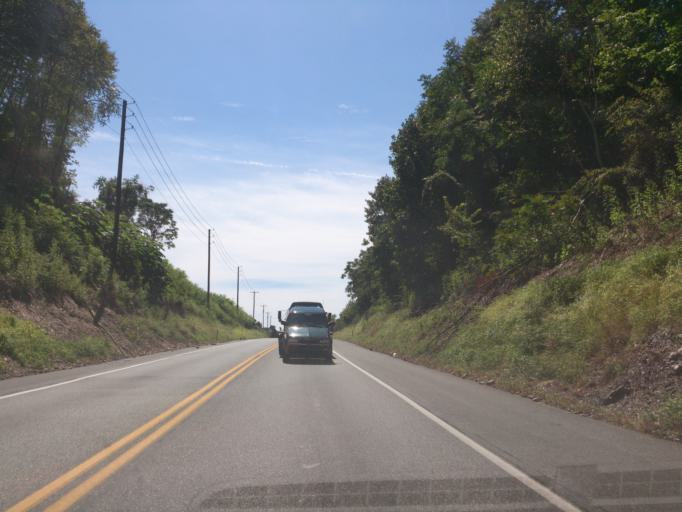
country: US
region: Pennsylvania
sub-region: Lancaster County
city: Columbia
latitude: 40.0494
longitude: -76.5157
